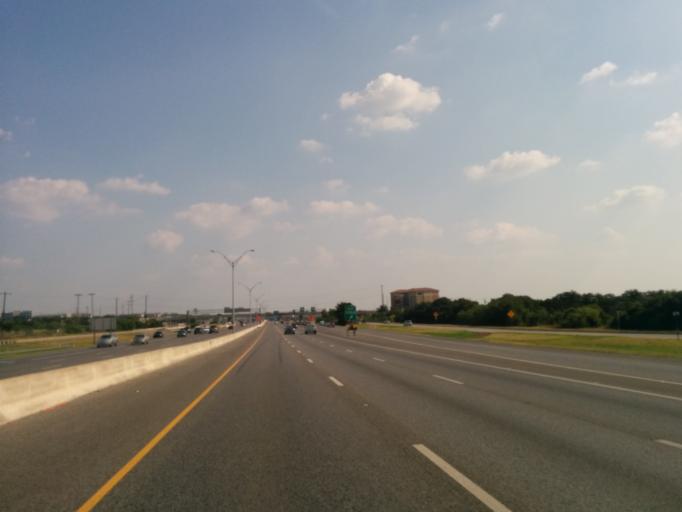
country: US
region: Texas
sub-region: Bexar County
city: Shavano Park
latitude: 29.5968
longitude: -98.5994
